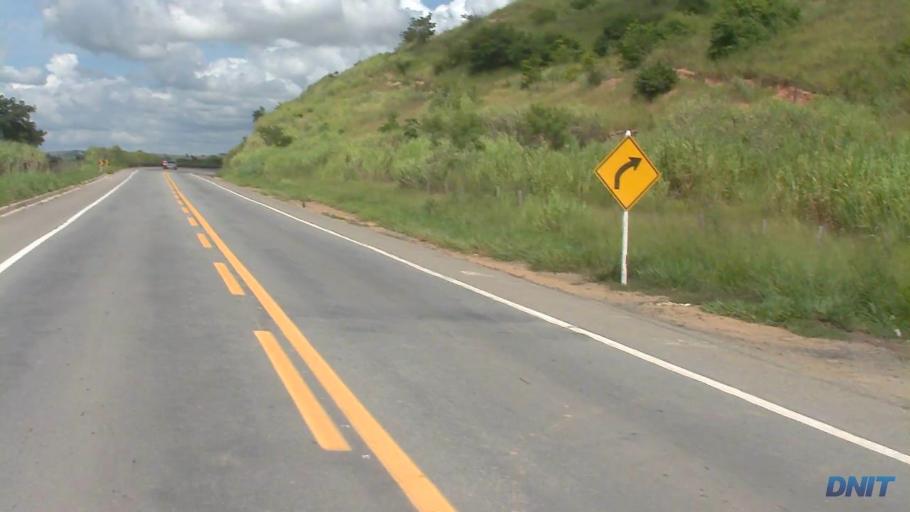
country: BR
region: Minas Gerais
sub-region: Governador Valadares
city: Governador Valadares
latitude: -18.9726
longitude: -42.0950
